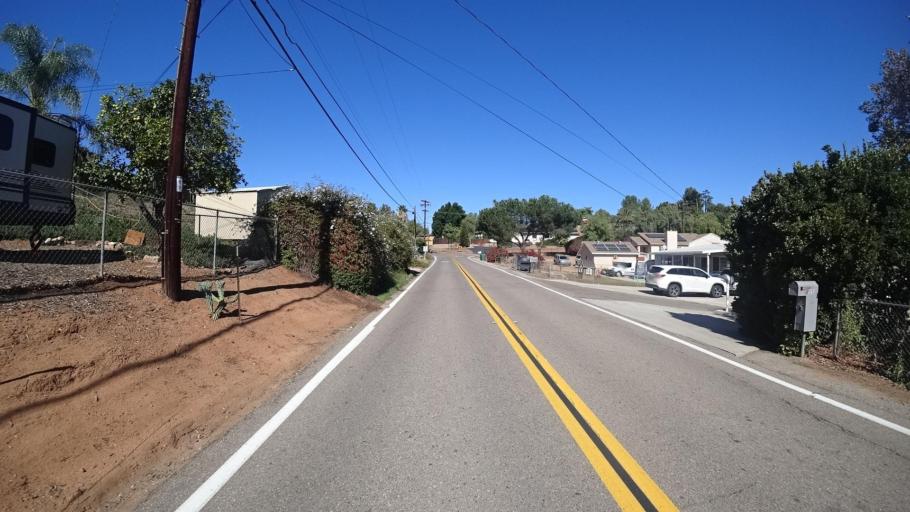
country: US
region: California
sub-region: San Diego County
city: Winter Gardens
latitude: 32.8436
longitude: -116.9367
